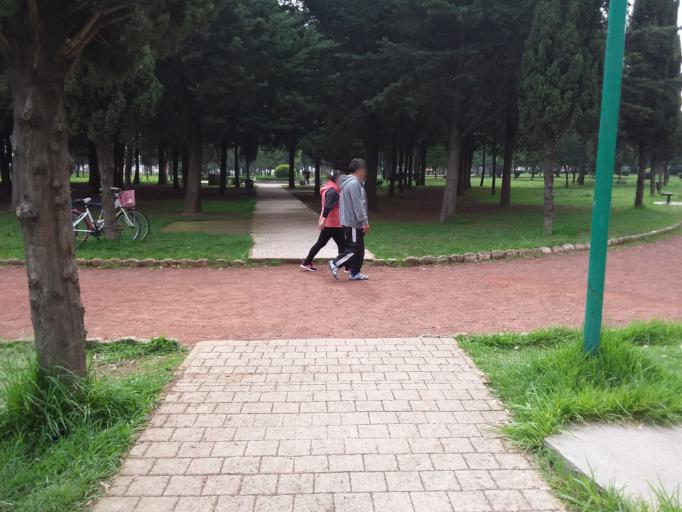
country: MX
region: Mexico
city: Toluca
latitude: 19.3164
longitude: -99.6502
